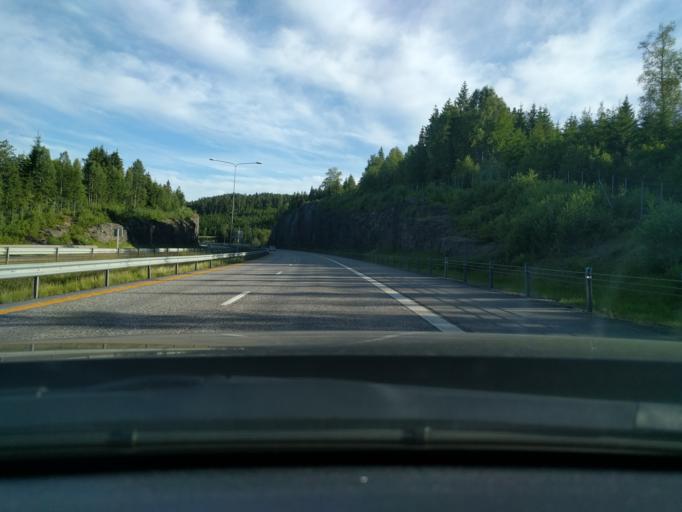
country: NO
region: Vestfold
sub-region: Sande
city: Sande
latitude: 59.5978
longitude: 10.1664
